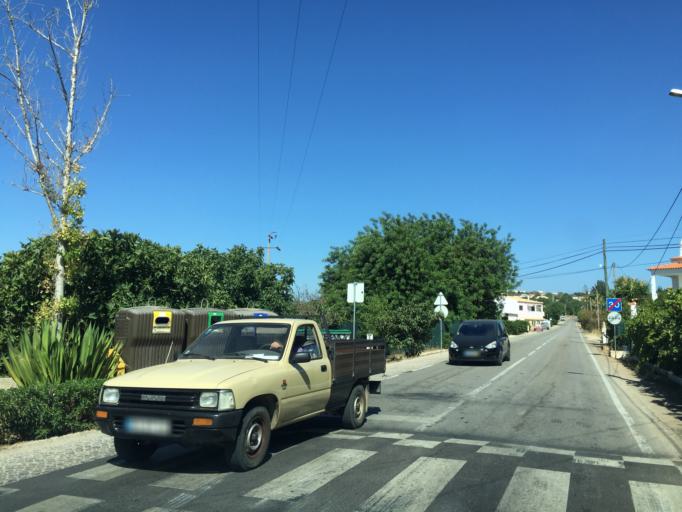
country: PT
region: Faro
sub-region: Loule
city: Vilamoura
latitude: 37.1117
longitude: -8.0888
